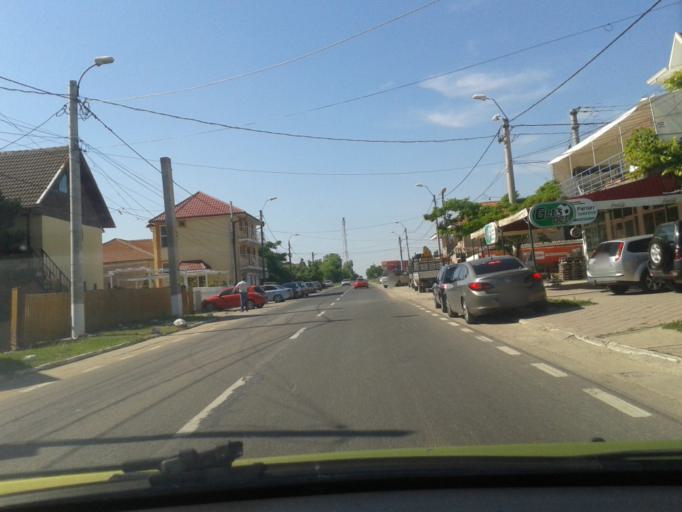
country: RO
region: Constanta
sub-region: Municipiul Mangalia
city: Mangalia
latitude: 43.7824
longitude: 28.5781
